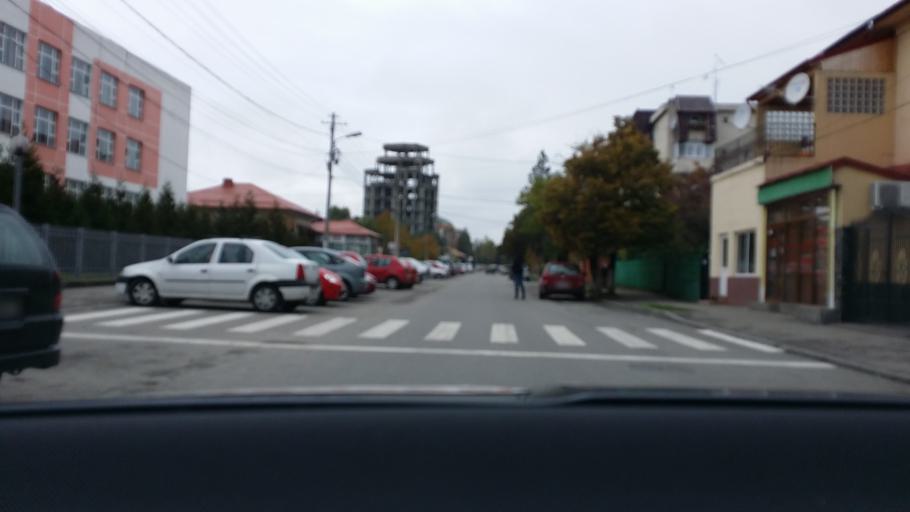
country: RO
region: Prahova
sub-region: Municipiul Campina
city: Campina
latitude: 45.1278
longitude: 25.7363
